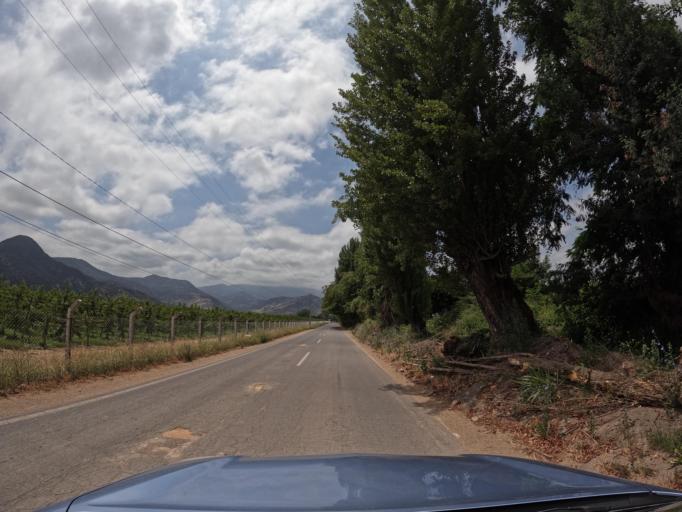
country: CL
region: O'Higgins
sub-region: Provincia de Colchagua
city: Chimbarongo
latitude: -34.7458
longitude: -70.9620
